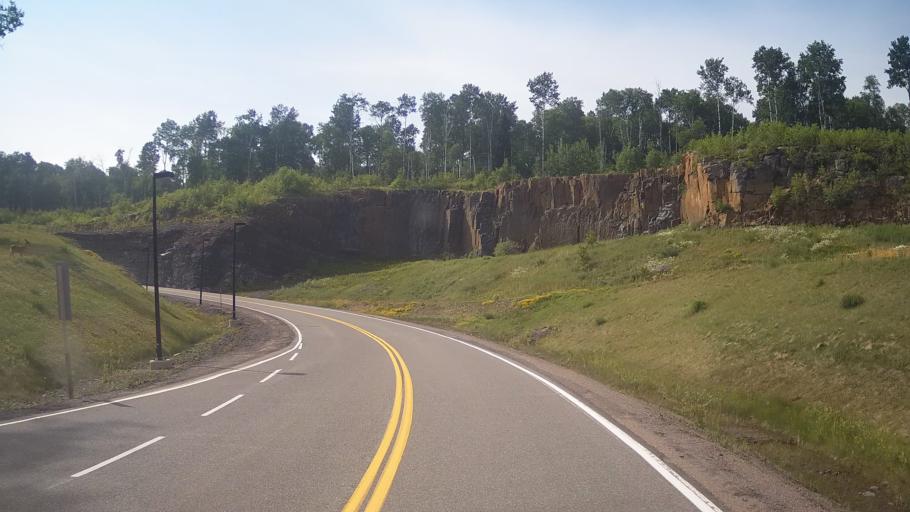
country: CA
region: Ontario
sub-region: Thunder Bay District
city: Thunder Bay
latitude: 48.4880
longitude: -89.1579
